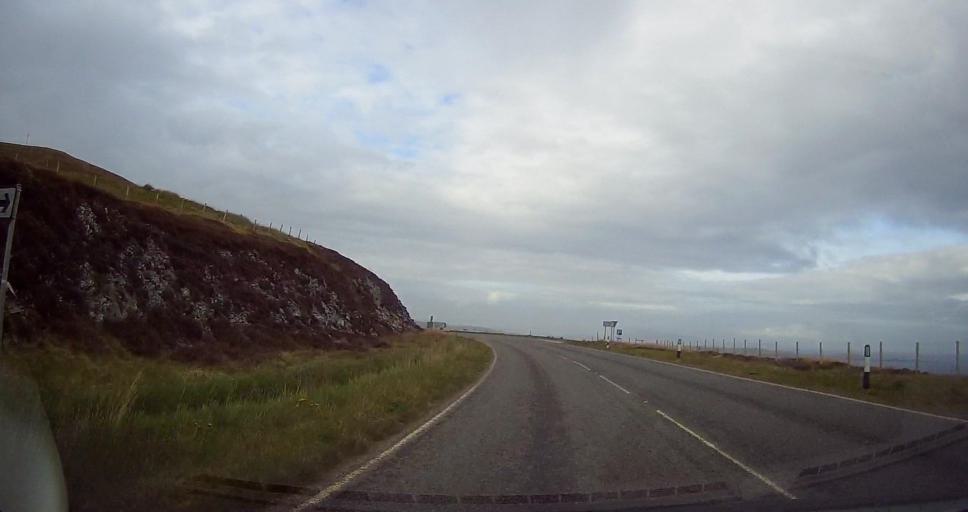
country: GB
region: Scotland
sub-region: Shetland Islands
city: Sandwick
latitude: 60.0168
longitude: -1.2319
